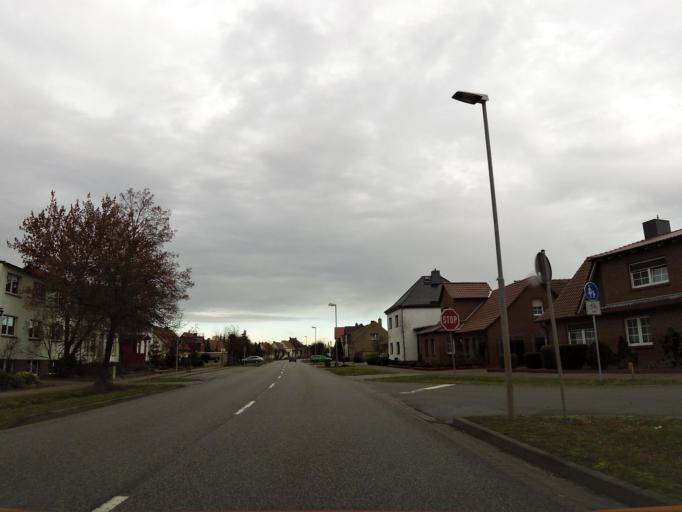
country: DE
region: Saxony-Anhalt
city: Letzlingen
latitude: 52.4396
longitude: 11.4835
